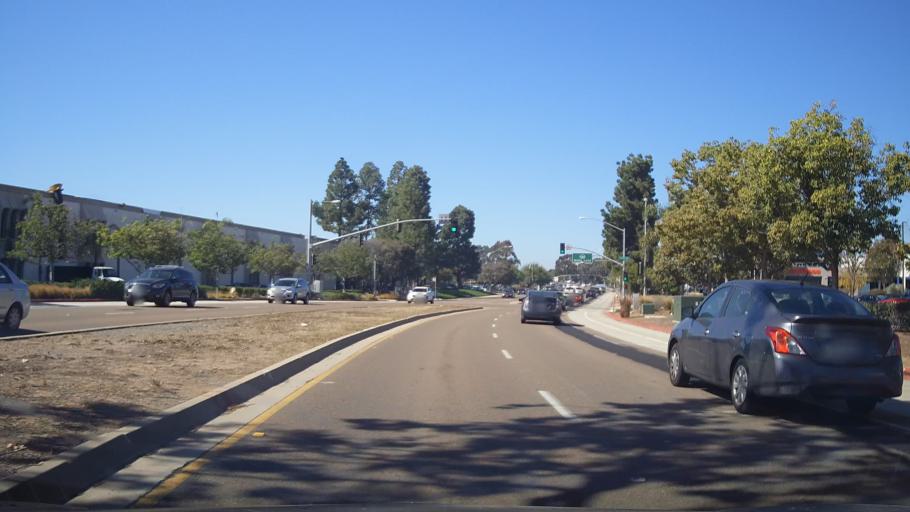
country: US
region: California
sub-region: San Diego County
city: San Diego
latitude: 32.8204
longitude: -117.1404
